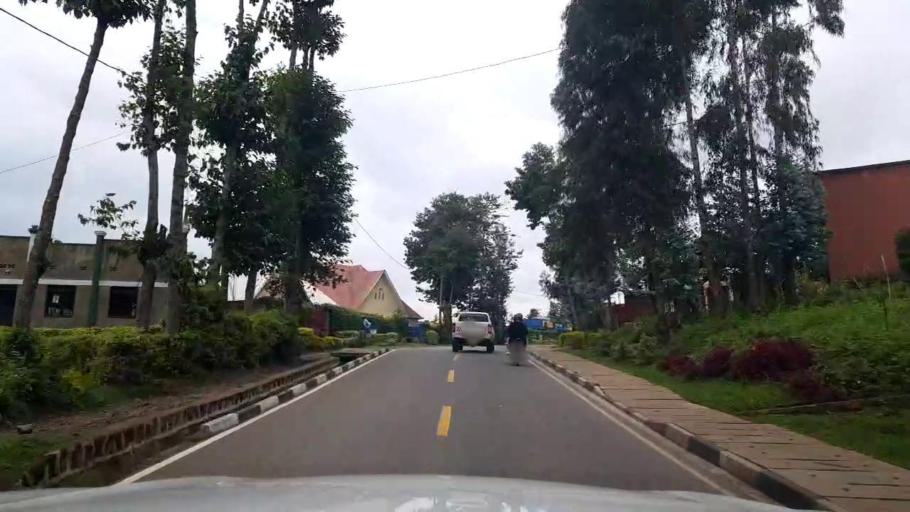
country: RW
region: Northern Province
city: Musanze
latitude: -1.4498
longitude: 29.5912
